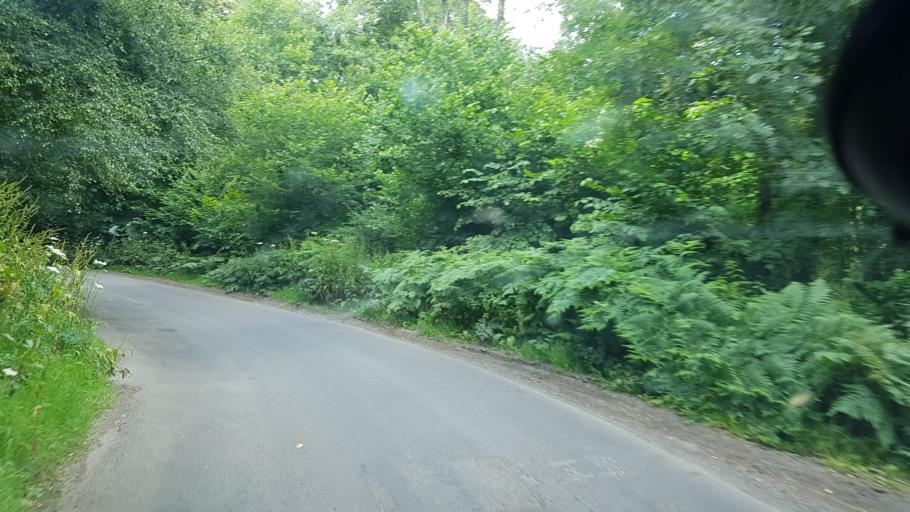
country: GB
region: England
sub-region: West Sussex
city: South Nutfield
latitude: 51.0599
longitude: -0.1209
